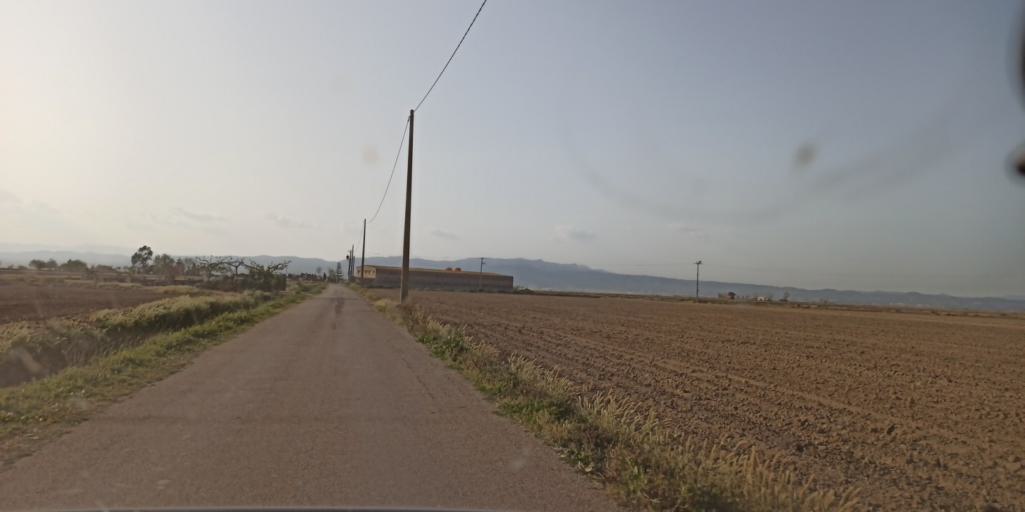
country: ES
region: Catalonia
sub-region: Provincia de Tarragona
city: Deltebre
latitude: 40.7523
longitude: 0.7583
